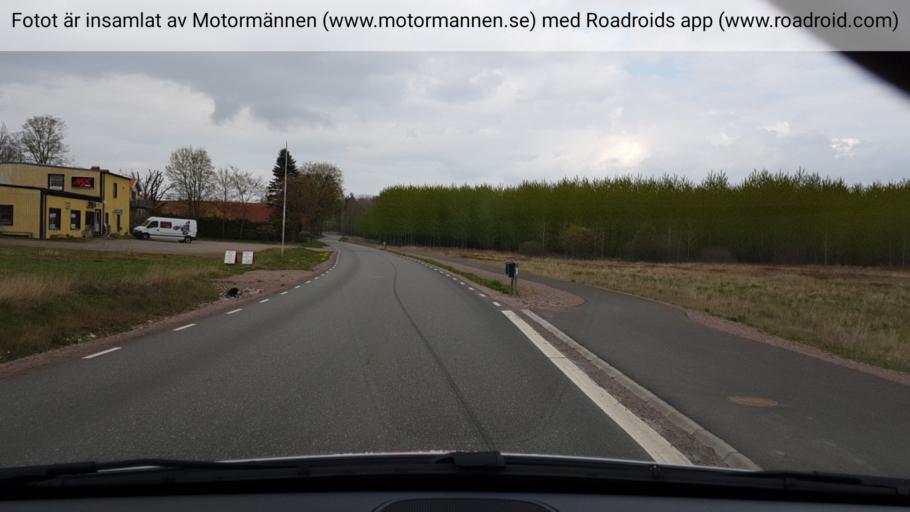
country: SE
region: Vaestra Goetaland
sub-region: Skovde Kommun
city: Stopen
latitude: 58.4650
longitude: 13.8634
